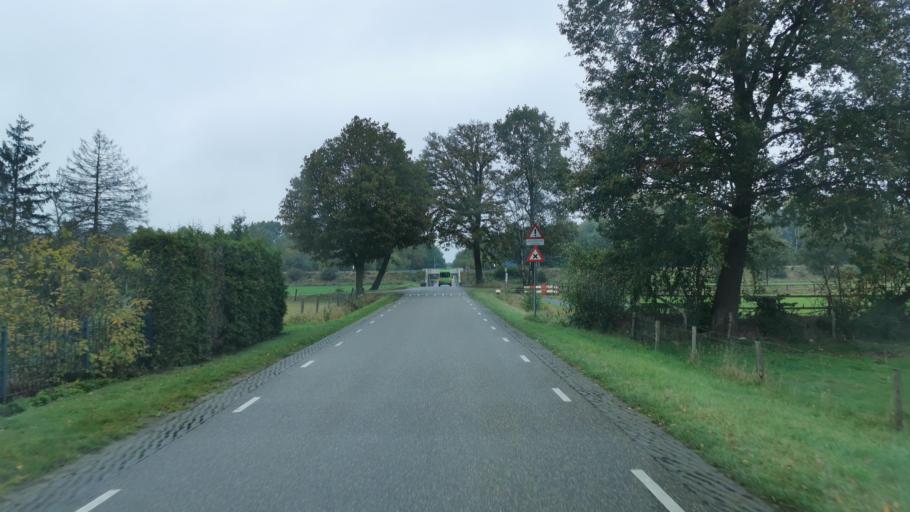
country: NL
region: Overijssel
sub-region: Gemeente Losser
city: Losser
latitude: 52.3066
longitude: 7.0161
